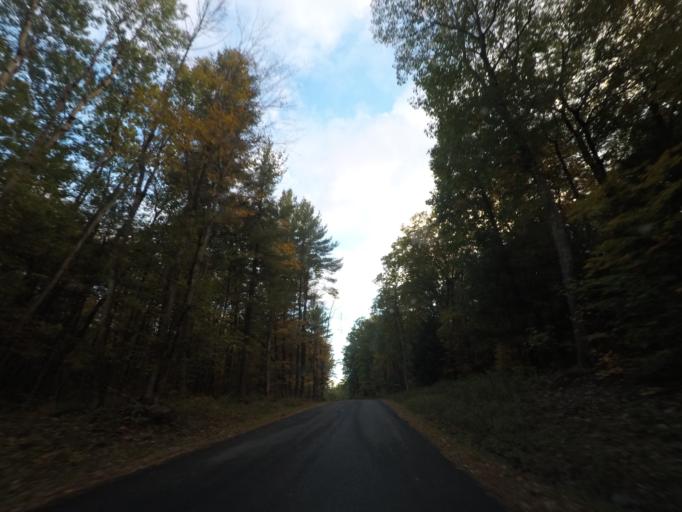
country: US
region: New York
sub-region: Rensselaer County
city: Nassau
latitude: 42.5434
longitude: -73.5787
